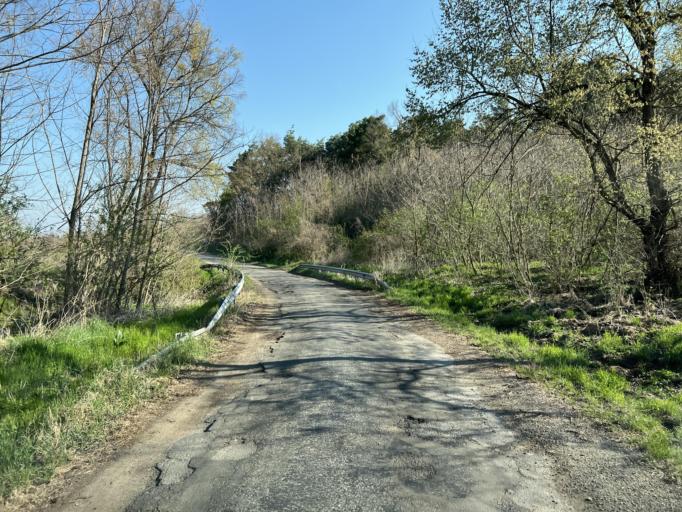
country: SK
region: Nitriansky
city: Sahy
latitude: 47.9946
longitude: 18.8184
